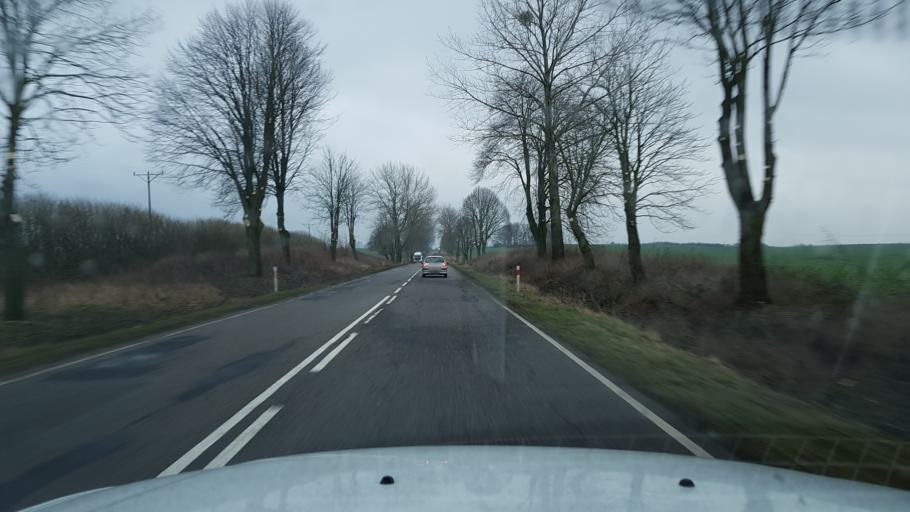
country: PL
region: West Pomeranian Voivodeship
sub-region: Powiat gryficki
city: Ploty
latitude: 53.8374
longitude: 15.2394
